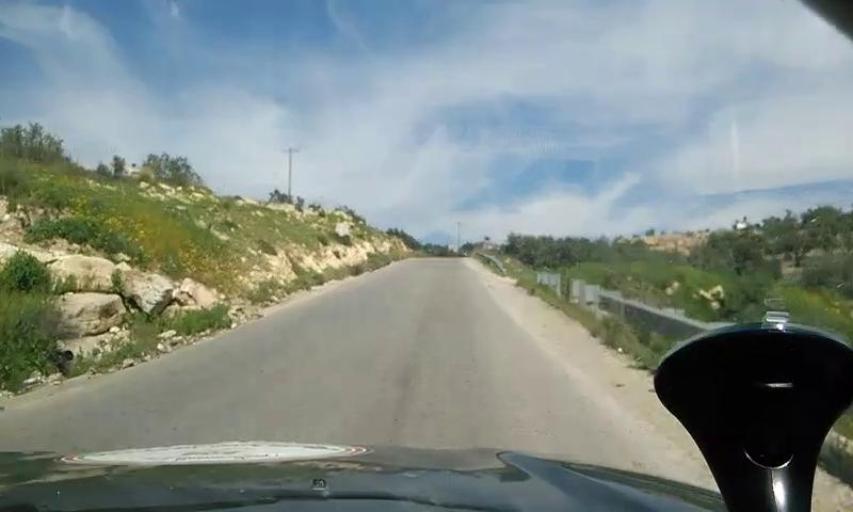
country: PS
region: West Bank
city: Kharbatha al Misbah
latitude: 31.8827
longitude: 35.0799
